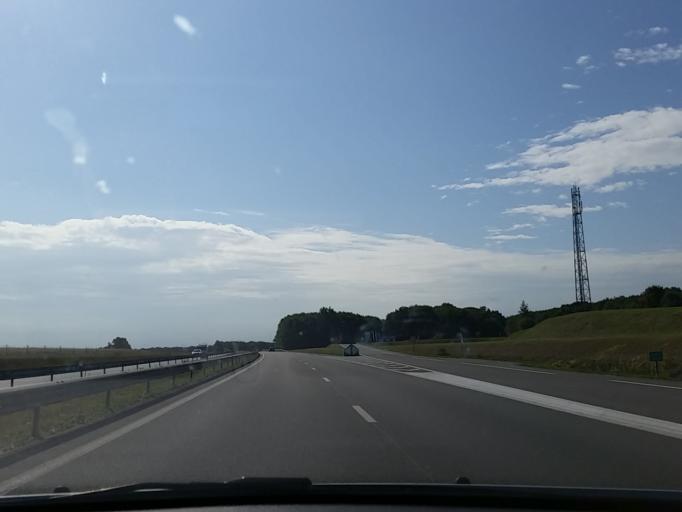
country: FR
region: Centre
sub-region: Departement du Cher
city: Plaimpied-Givaudins
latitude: 46.9851
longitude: 2.4137
